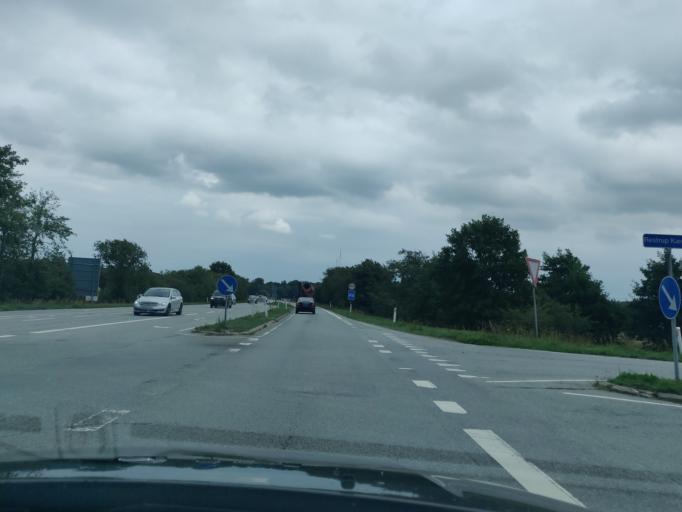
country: DK
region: North Denmark
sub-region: Alborg Kommune
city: Frejlev
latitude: 57.0108
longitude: 9.7749
